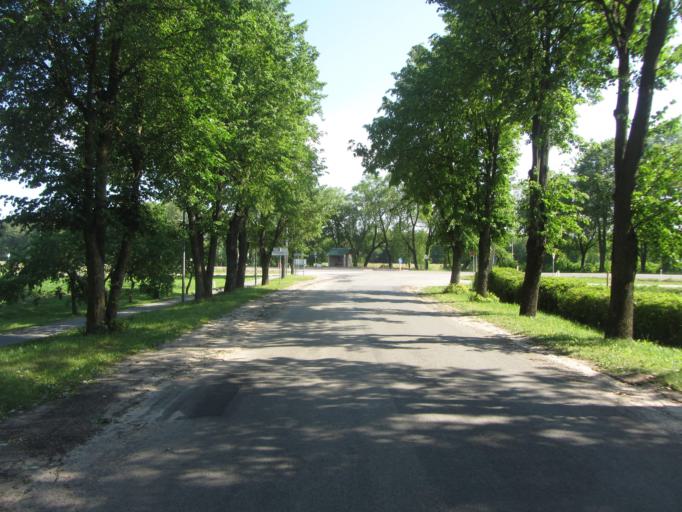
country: LT
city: Birstonas
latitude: 54.5929
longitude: 24.0288
